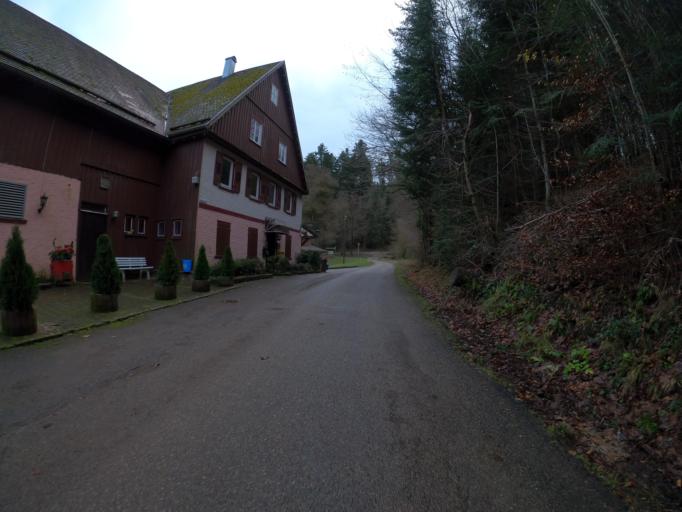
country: DE
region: Baden-Wuerttemberg
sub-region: Regierungsbezirk Stuttgart
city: Waschenbeuren
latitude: 48.7719
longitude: 9.7129
